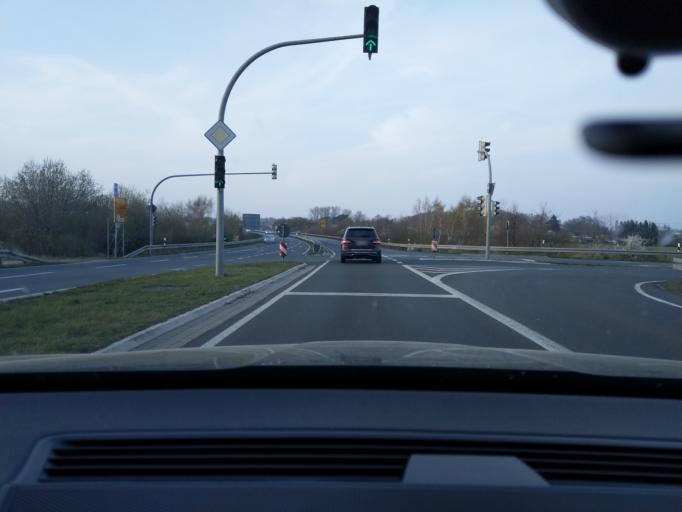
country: DE
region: Mecklenburg-Vorpommern
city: Stralsund
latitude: 54.2954
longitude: 13.0515
